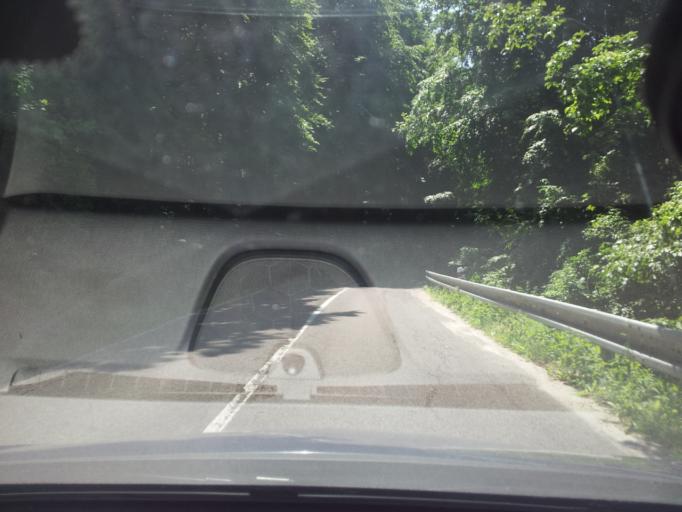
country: SK
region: Nitriansky
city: Partizanske
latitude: 48.5381
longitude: 18.4455
